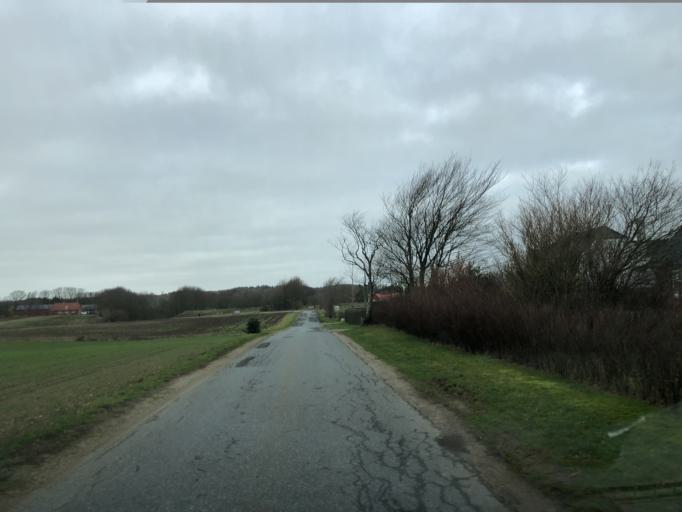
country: DK
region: Central Jutland
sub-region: Viborg Kommune
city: Stoholm
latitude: 56.4539
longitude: 9.1300
